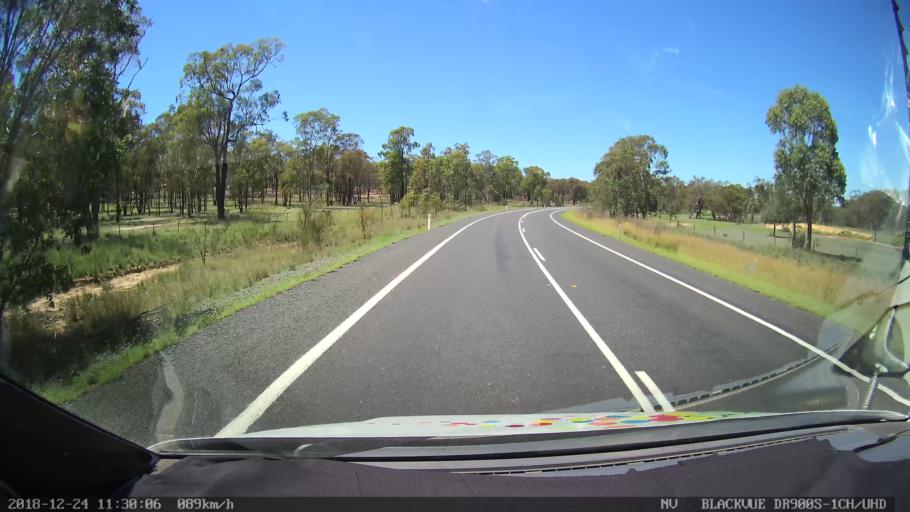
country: AU
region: New South Wales
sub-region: Upper Hunter Shire
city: Merriwa
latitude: -32.2005
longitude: 150.4671
